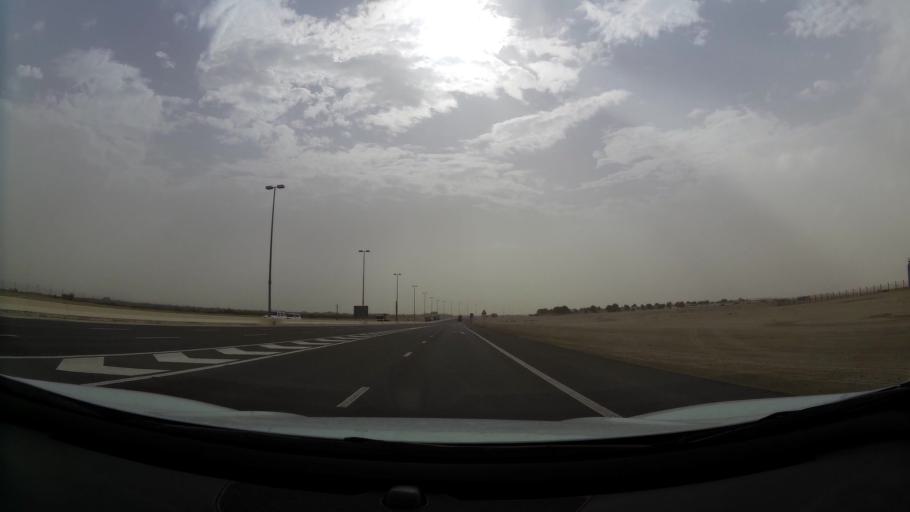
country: AE
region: Abu Dhabi
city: Abu Dhabi
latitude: 24.4770
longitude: 54.6655
